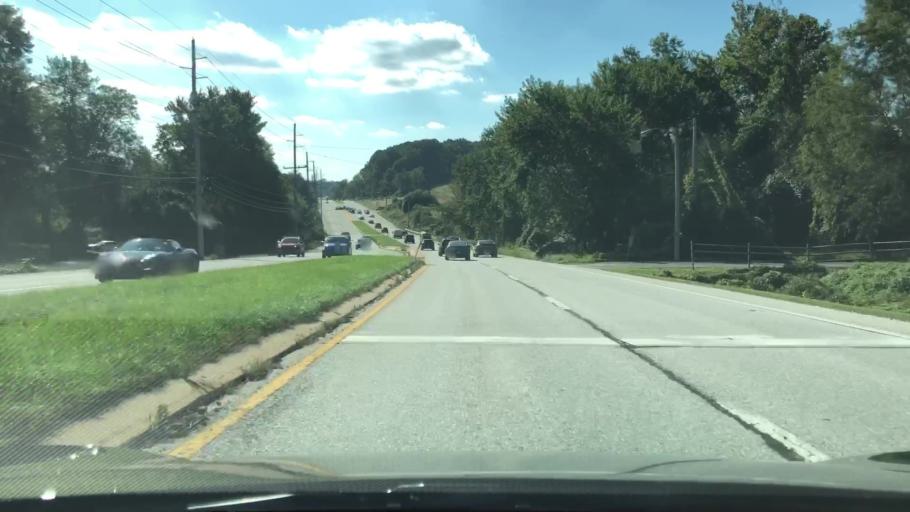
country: US
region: Pennsylvania
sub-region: Delaware County
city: Lima
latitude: 39.9708
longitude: -75.4705
